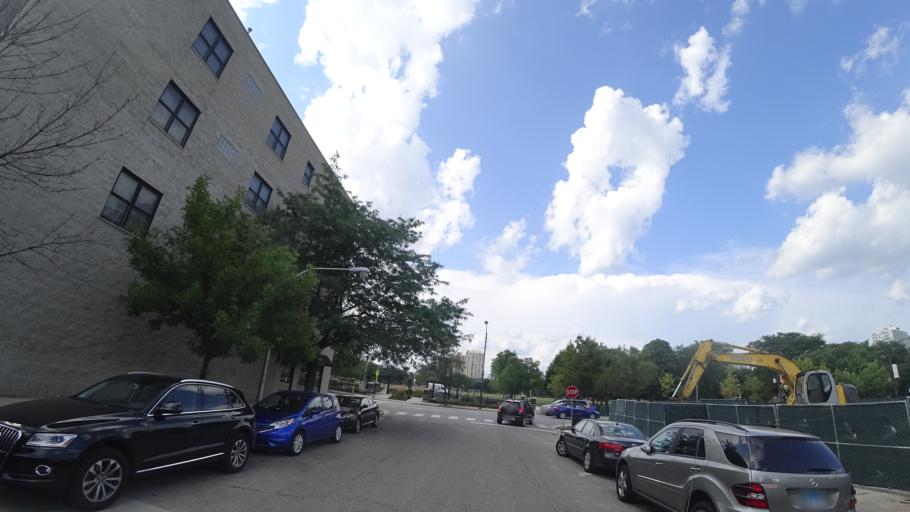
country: US
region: Illinois
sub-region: Cook County
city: Chicago
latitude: 41.8380
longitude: -87.6206
